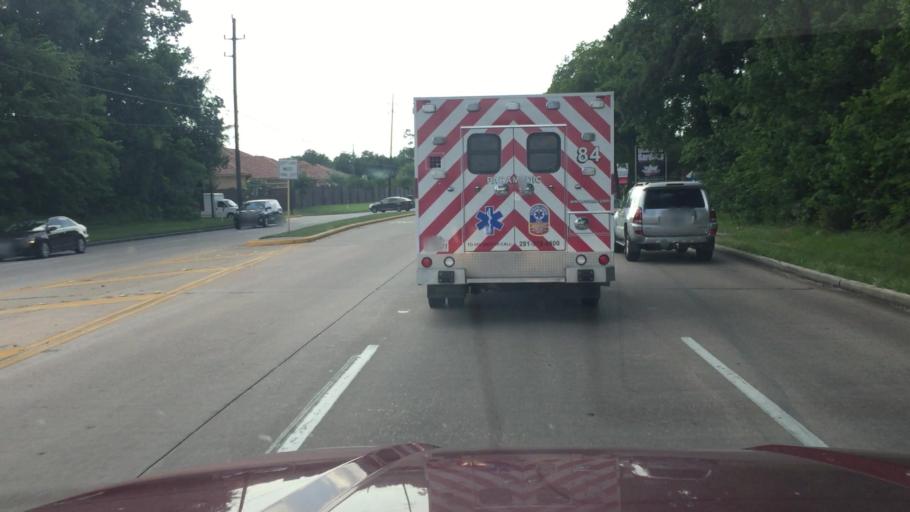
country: US
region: Texas
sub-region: Harris County
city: Tomball
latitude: 30.0240
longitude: -95.5275
